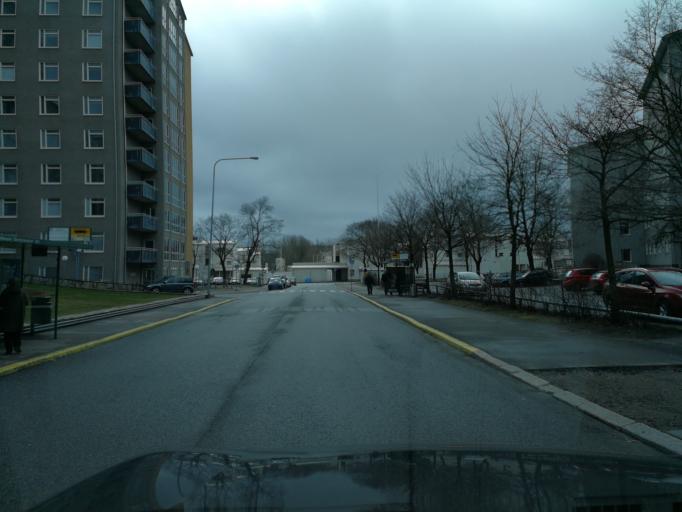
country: FI
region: Uusimaa
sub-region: Helsinki
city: Helsinki
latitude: 60.2042
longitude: 24.9503
